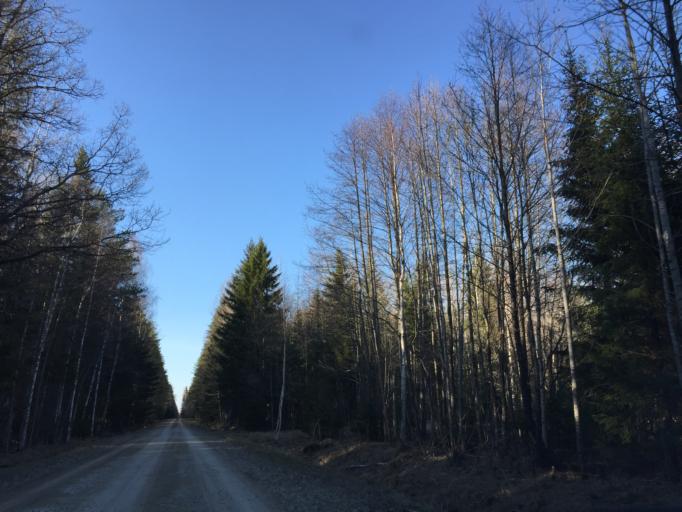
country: EE
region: Ida-Virumaa
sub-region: Sillamaee linn
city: Sillamae
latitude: 59.1579
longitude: 27.8012
